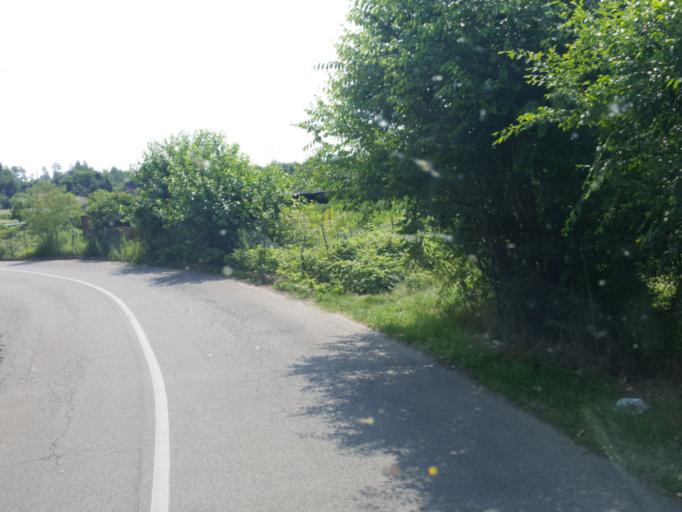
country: IT
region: Lombardy
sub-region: Provincia di Varese
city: Castiglione Olona
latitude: 45.7418
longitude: 8.8743
